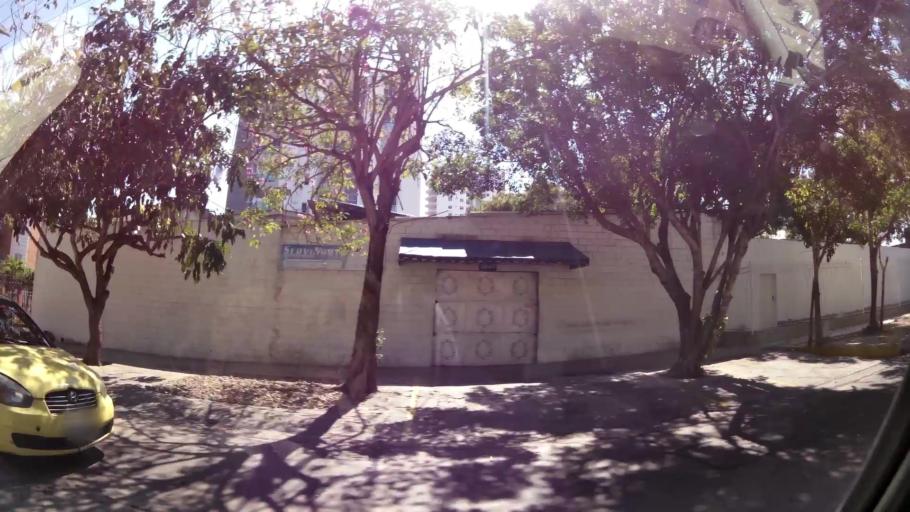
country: CO
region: Atlantico
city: Barranquilla
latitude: 11.0087
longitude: -74.8163
